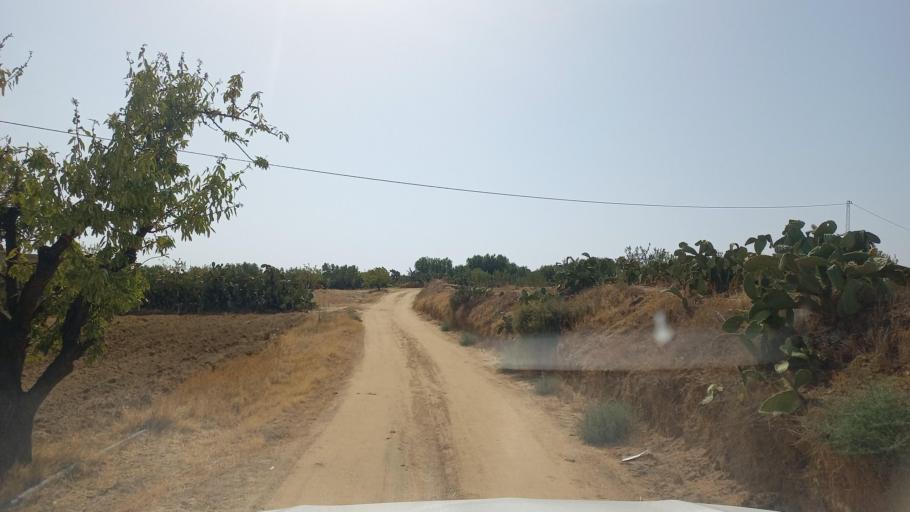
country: TN
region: Al Qasrayn
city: Kasserine
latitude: 35.2369
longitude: 9.0546
